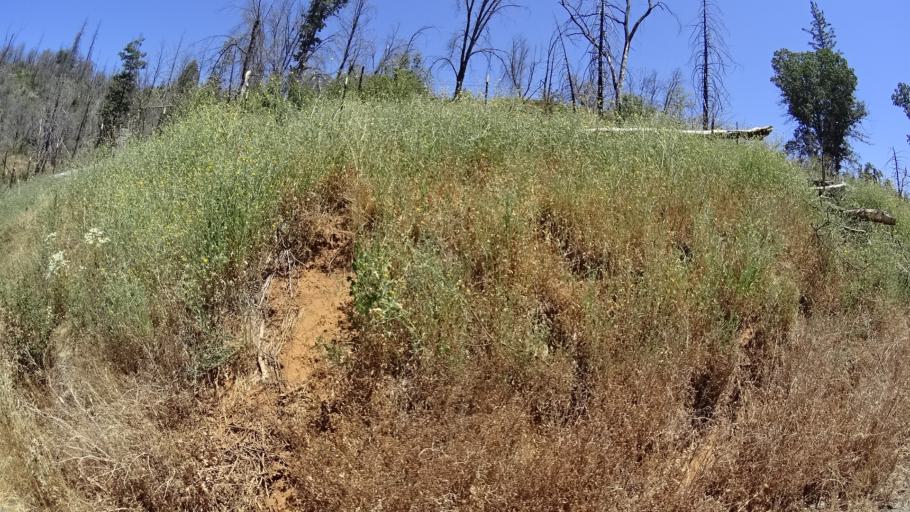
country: US
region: California
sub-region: Calaveras County
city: Mountain Ranch
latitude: 38.2598
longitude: -120.5817
